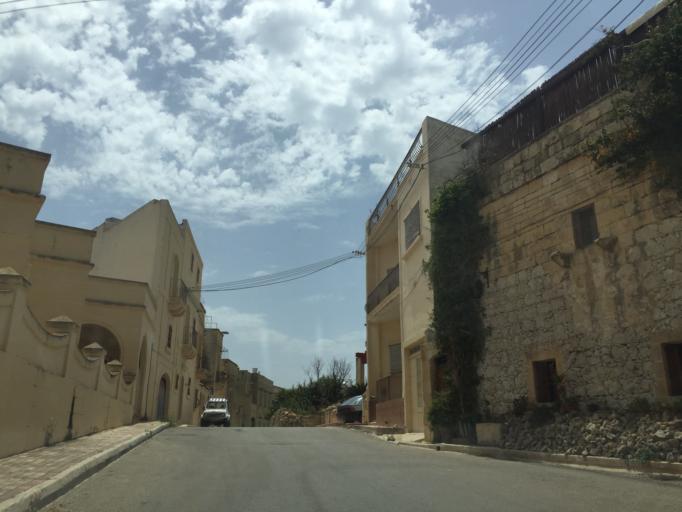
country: MT
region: Ix-Xaghra
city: Xaghra
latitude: 36.0536
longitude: 14.2713
